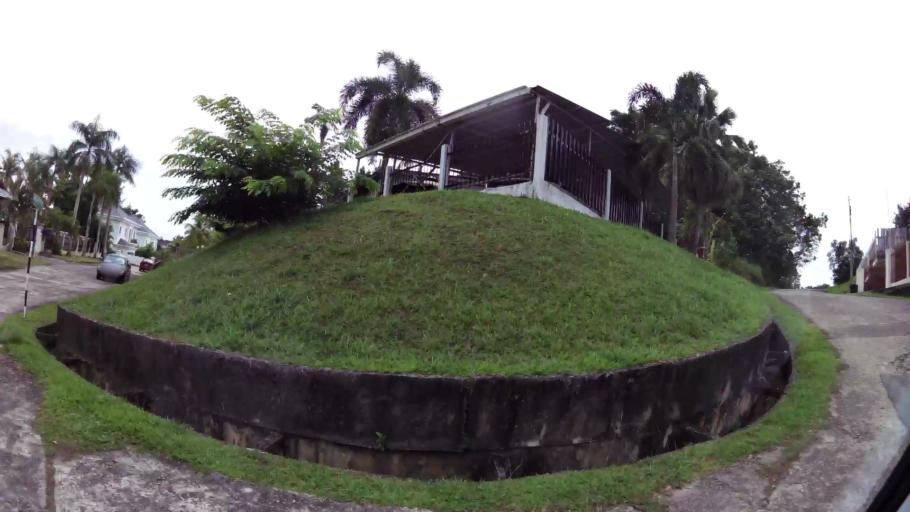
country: BN
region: Brunei and Muara
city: Bandar Seri Begawan
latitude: 4.8877
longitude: 114.9173
